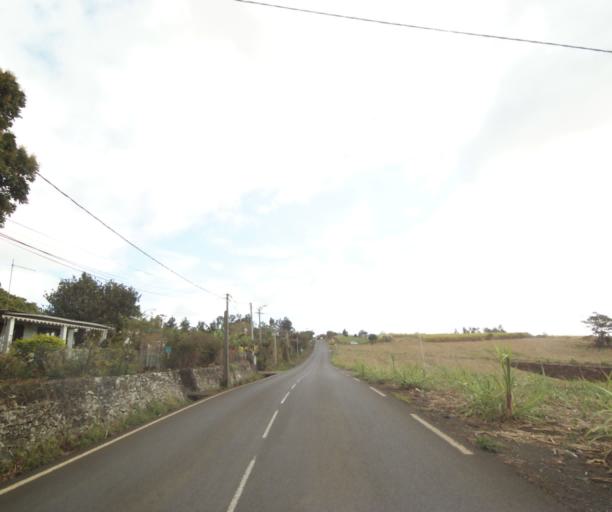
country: RE
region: Reunion
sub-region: Reunion
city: Trois-Bassins
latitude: -21.0652
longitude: 55.2790
